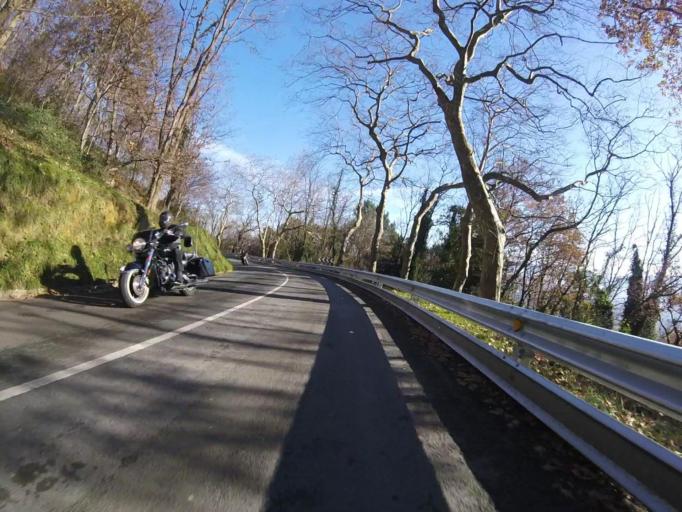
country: ES
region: Basque Country
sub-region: Provincia de Guipuzcoa
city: Fuenterrabia
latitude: 43.3671
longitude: -1.8196
